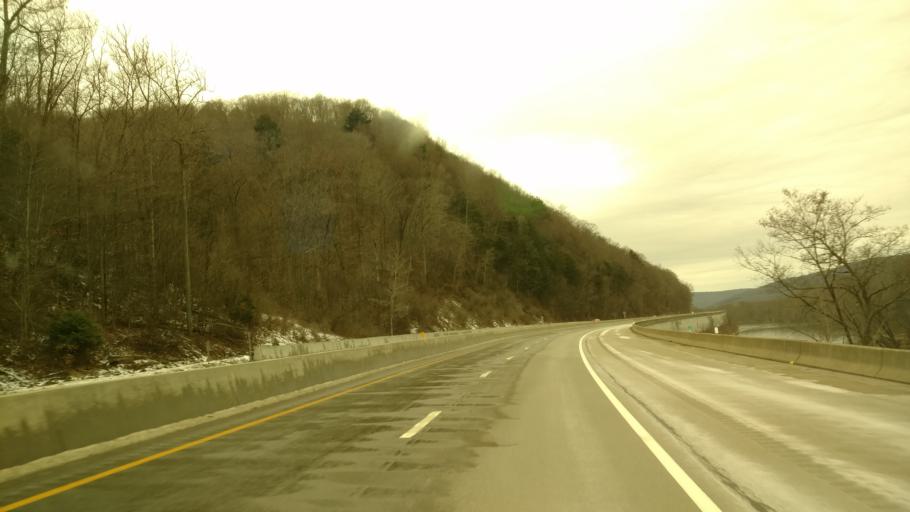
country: US
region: New York
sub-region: Cattaraugus County
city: Salamanca
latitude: 42.1481
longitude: -78.6853
